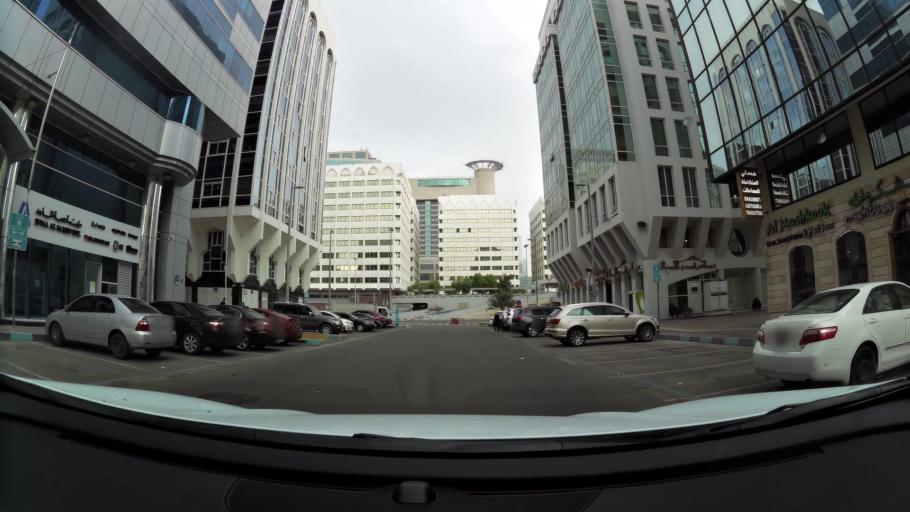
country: AE
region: Abu Dhabi
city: Abu Dhabi
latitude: 24.4935
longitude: 54.3814
